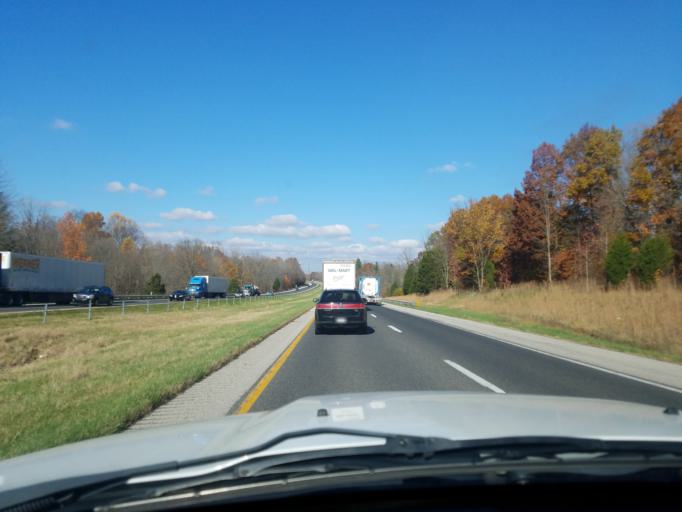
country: US
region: Indiana
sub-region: Jackson County
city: Seymour
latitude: 39.0762
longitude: -85.9281
